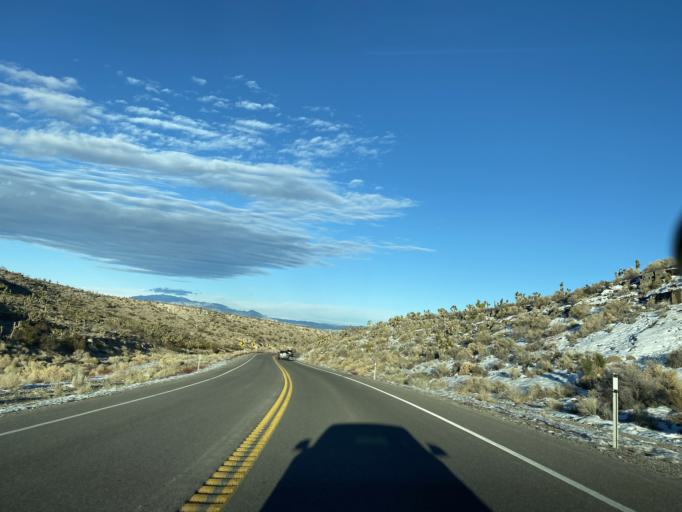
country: US
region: Nevada
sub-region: Clark County
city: Summerlin South
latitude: 36.2777
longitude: -115.4689
